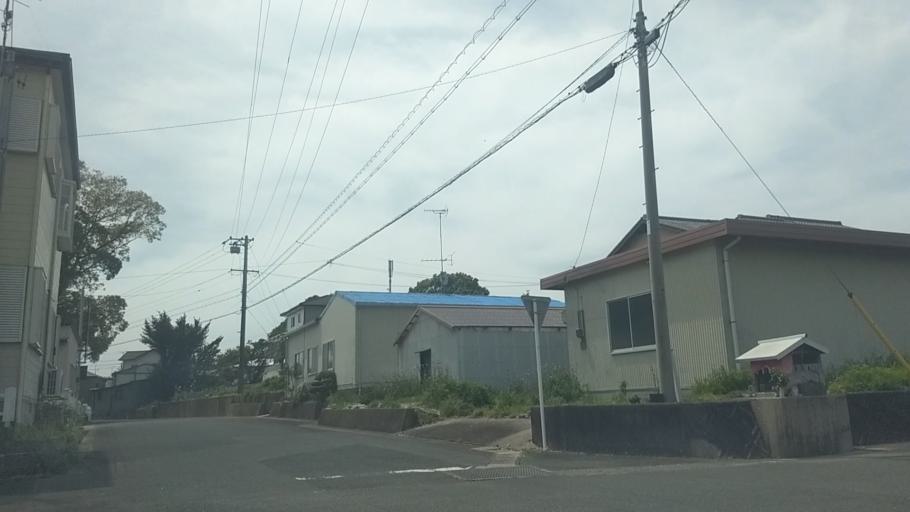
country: JP
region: Shizuoka
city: Kosai-shi
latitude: 34.7534
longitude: 137.5286
